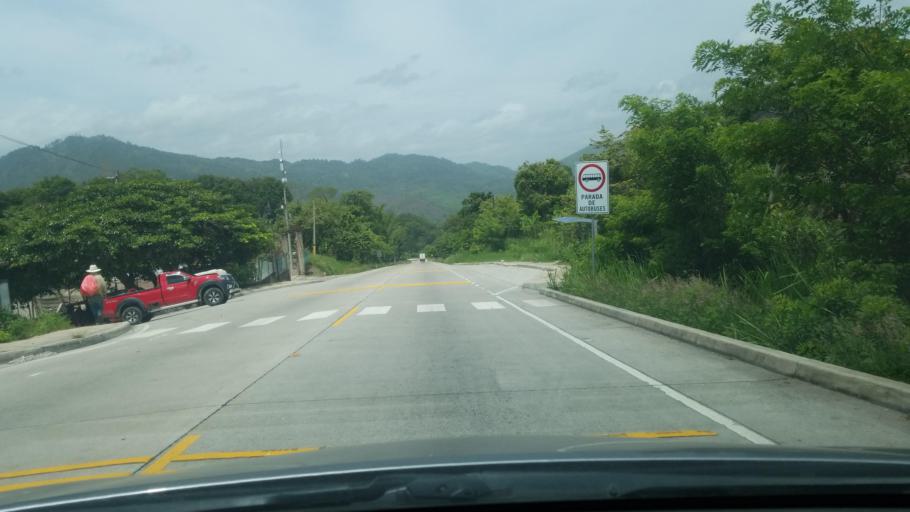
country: HN
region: Copan
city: Quezailica
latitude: 14.9078
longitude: -88.7526
